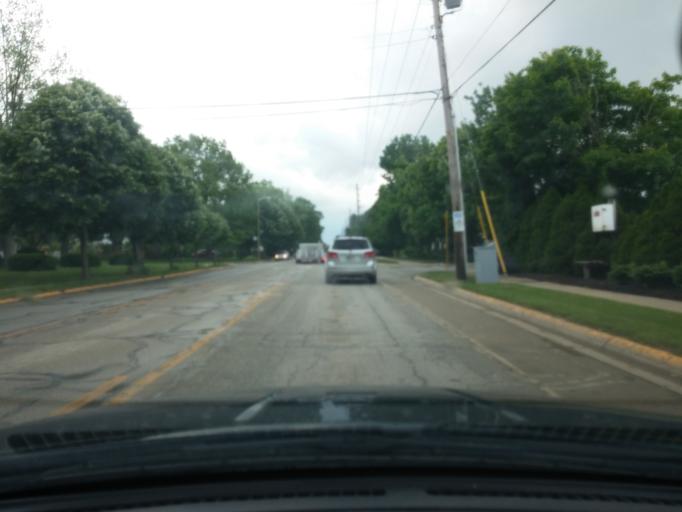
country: US
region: Indiana
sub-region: Tippecanoe County
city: West Lafayette
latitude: 40.4588
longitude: -86.9157
